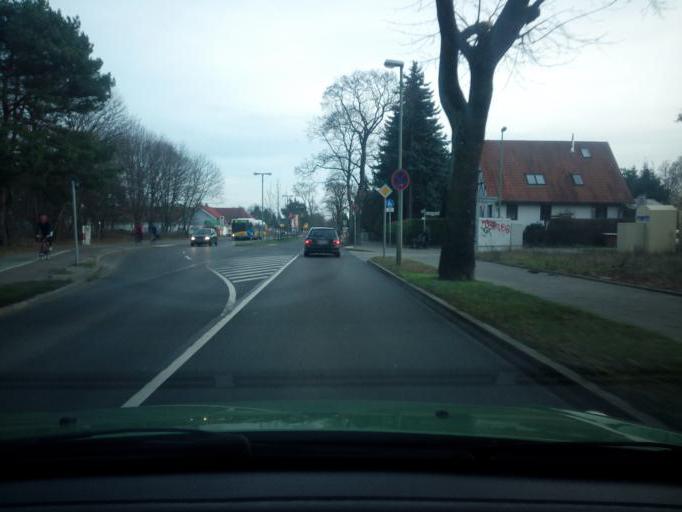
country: DE
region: Berlin
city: Muggelheim
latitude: 52.4157
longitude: 13.6555
